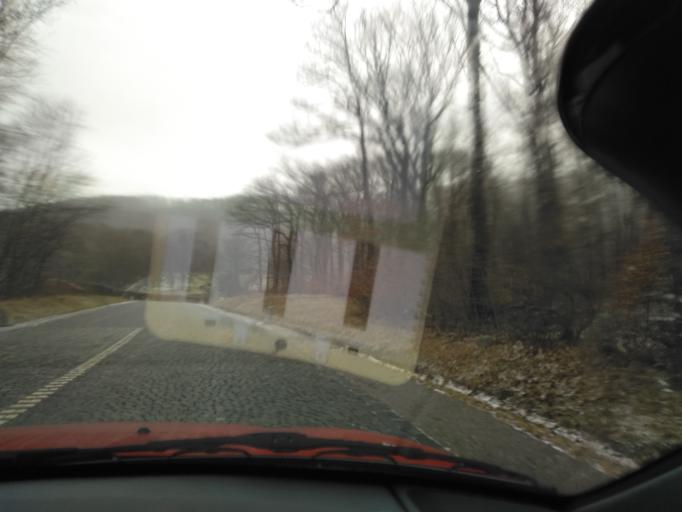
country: AT
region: Lower Austria
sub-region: Politischer Bezirk Wien-Umgebung
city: Klosterneuburg
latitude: 48.2644
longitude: 16.2953
